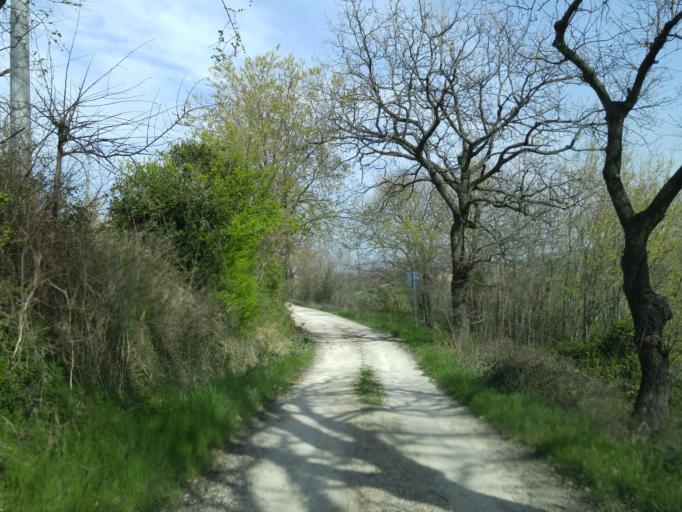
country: IT
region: The Marches
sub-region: Provincia di Pesaro e Urbino
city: Villanova
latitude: 43.7229
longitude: 12.9323
